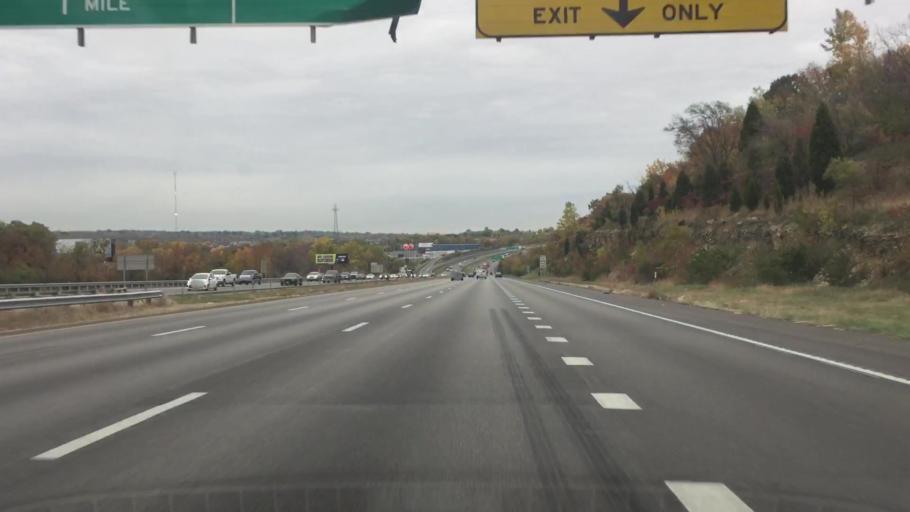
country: US
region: Missouri
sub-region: Jackson County
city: Raytown
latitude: 39.0412
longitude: -94.4998
